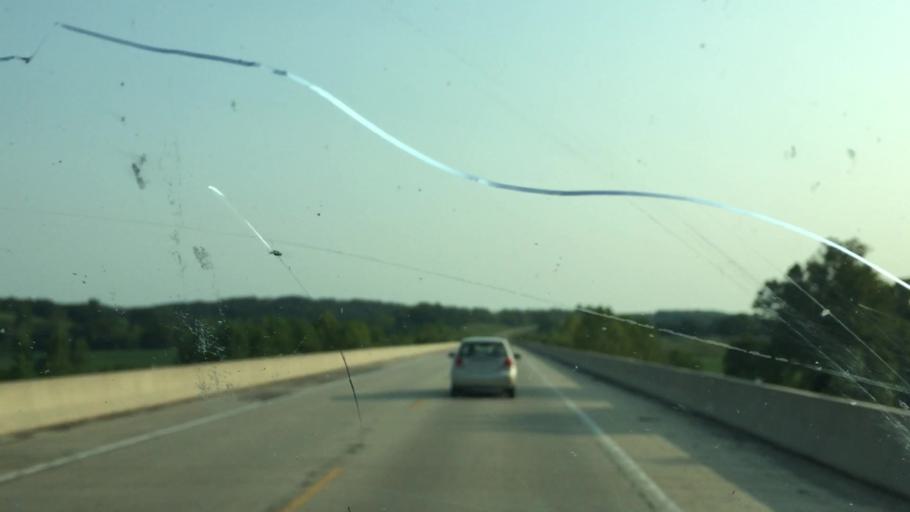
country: US
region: Missouri
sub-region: Pulaski County
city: Richland
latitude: 37.7987
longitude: -92.4058
